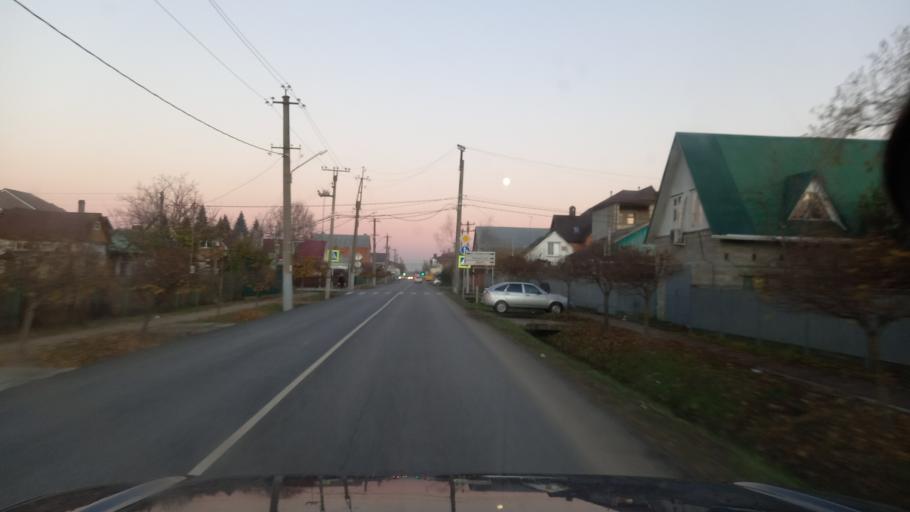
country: RU
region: Krasnodarskiy
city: Goryachiy Klyuch
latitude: 44.6280
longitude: 39.1026
